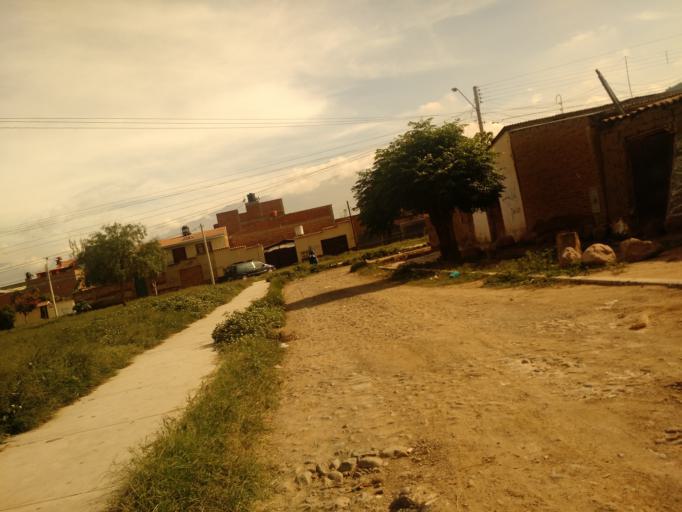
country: BO
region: Cochabamba
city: Cochabamba
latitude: -17.4355
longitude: -66.1575
